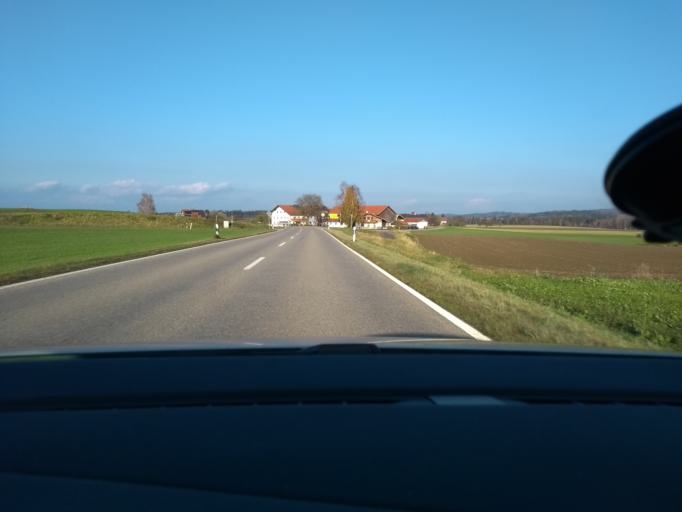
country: DE
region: Bavaria
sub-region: Upper Bavaria
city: Schonstett
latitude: 47.9803
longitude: 12.2619
